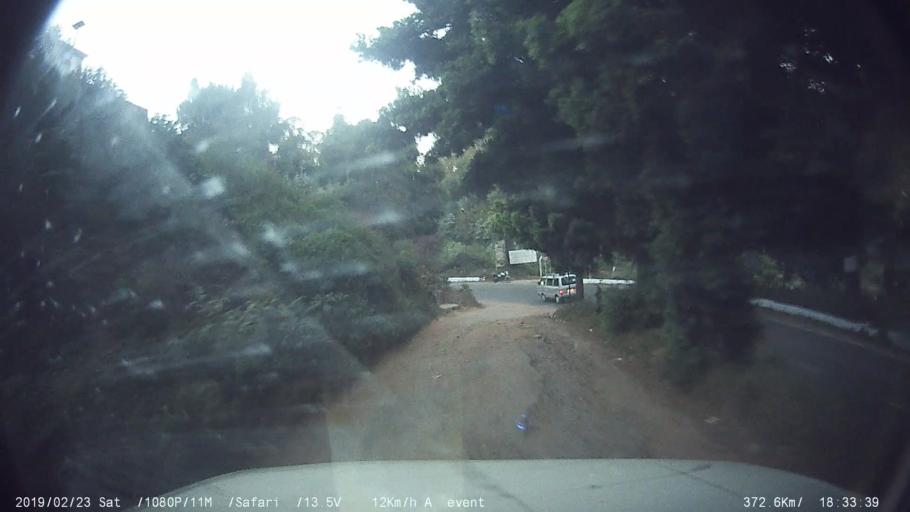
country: IN
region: Tamil Nadu
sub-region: Nilgiri
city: Wellington
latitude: 11.3516
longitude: 76.7856
